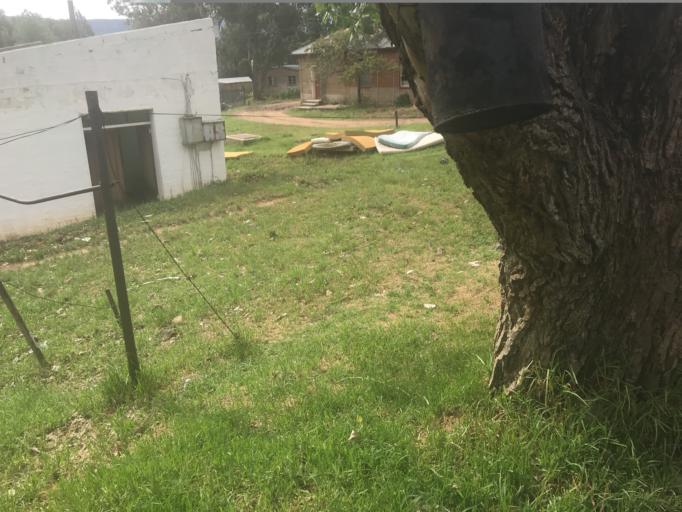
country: LS
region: Maseru
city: Nako
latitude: -29.6317
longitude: 27.5009
